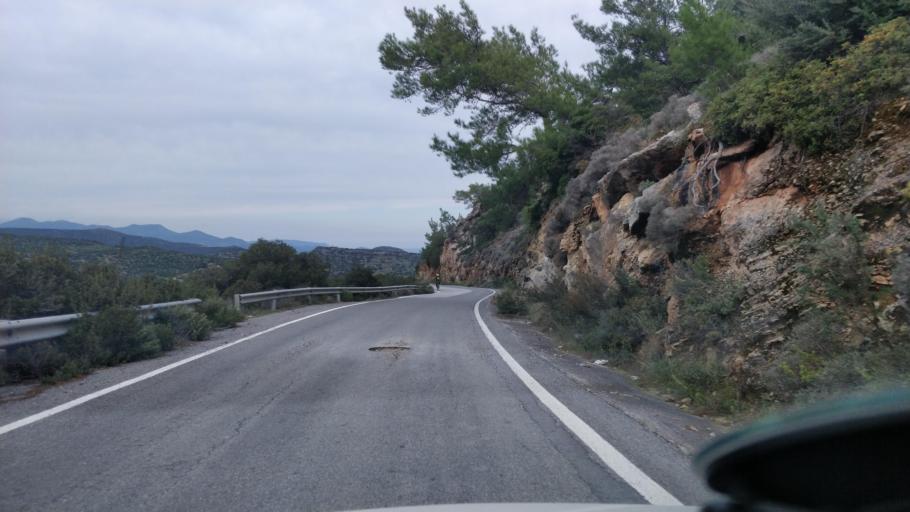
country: GR
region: Crete
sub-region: Nomos Lasithiou
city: Kritsa
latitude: 35.1055
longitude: 25.7115
